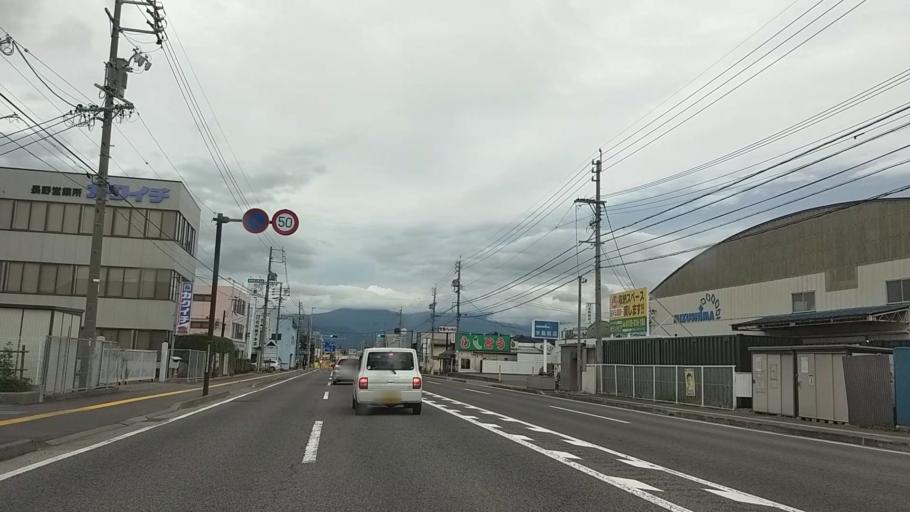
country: JP
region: Nagano
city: Nagano-shi
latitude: 36.6479
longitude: 138.2121
